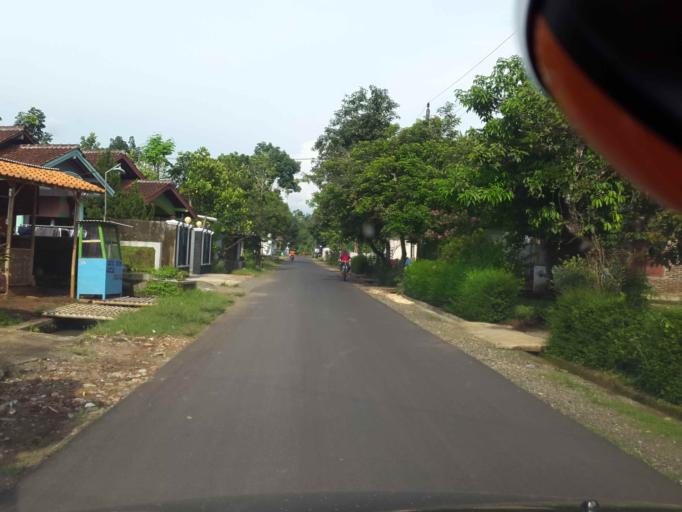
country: ID
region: Central Java
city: Purbalingga
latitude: -7.4615
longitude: 109.4882
